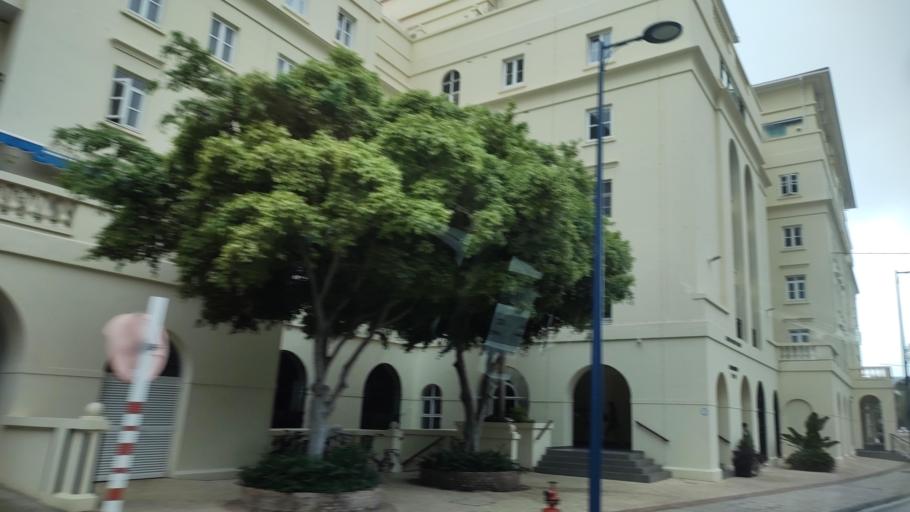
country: GI
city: Gibraltar
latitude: 36.1347
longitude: -5.3541
